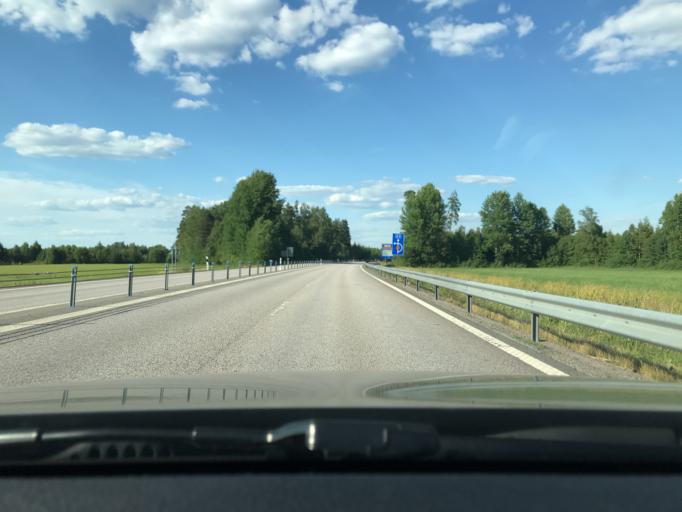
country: SE
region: Kronoberg
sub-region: Alvesta Kommun
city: Vislanda
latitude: 56.7630
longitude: 14.5252
